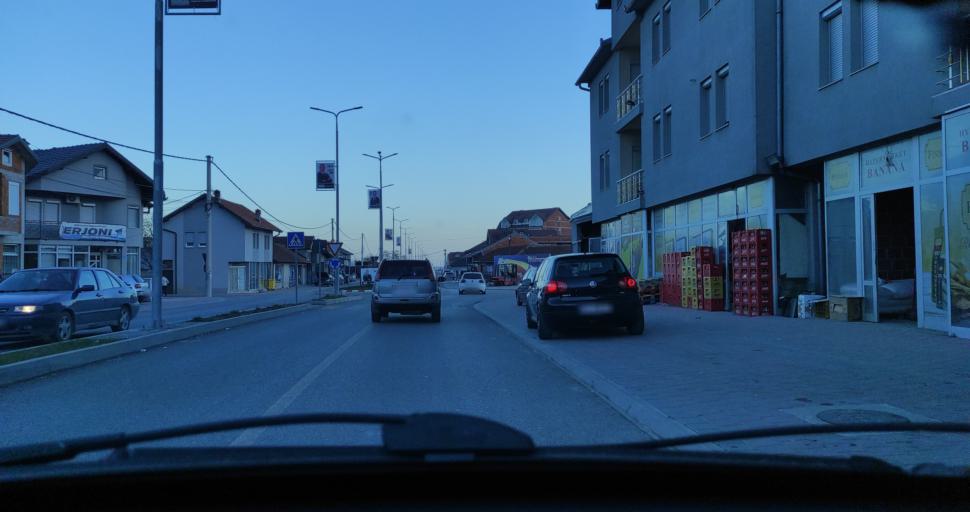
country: XK
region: Gjakova
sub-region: Komuna e Decanit
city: Decan
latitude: 42.5296
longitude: 20.2964
